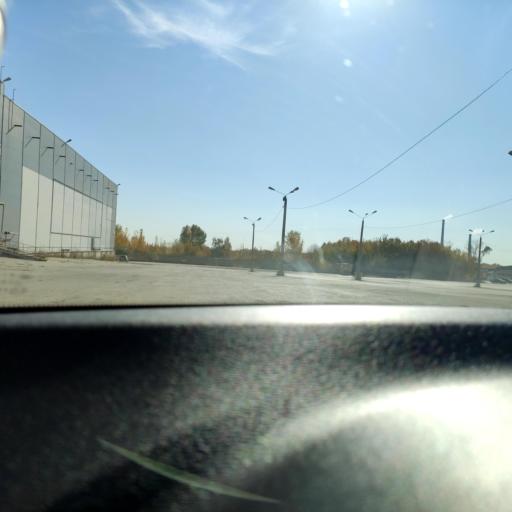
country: RU
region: Samara
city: Petra-Dubrava
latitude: 53.2733
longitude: 50.2738
